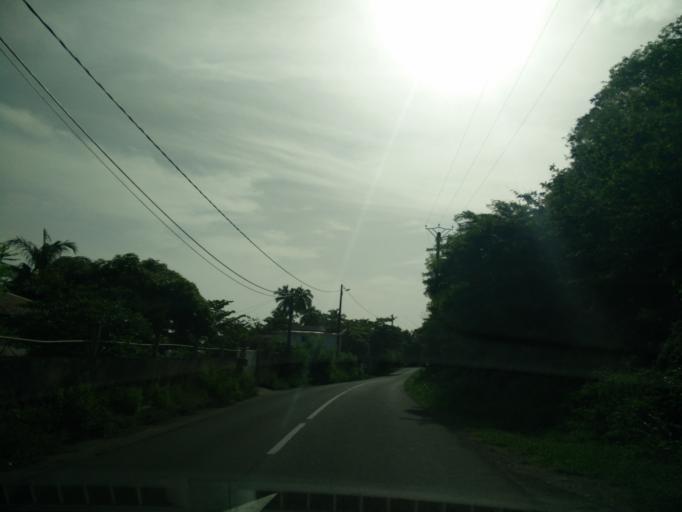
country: MQ
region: Martinique
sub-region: Martinique
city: Saint-Pierre
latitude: 14.7819
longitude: -61.2115
